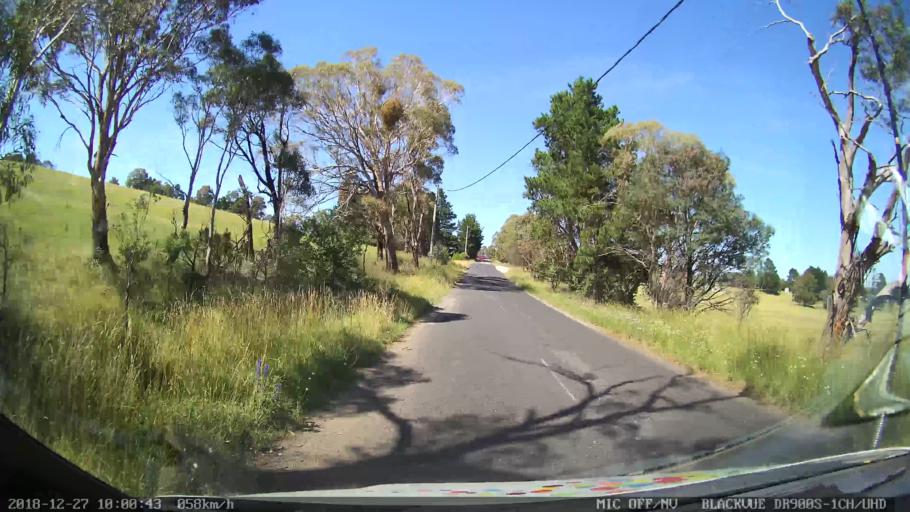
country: AU
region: New South Wales
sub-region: Lithgow
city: Portland
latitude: -33.4389
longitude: 149.9430
